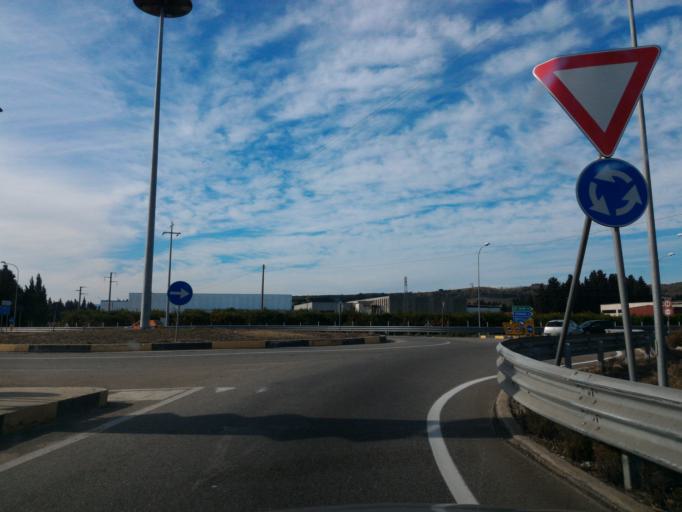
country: IT
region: Calabria
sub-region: Provincia di Catanzaro
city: Barone
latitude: 38.8585
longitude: 16.6752
